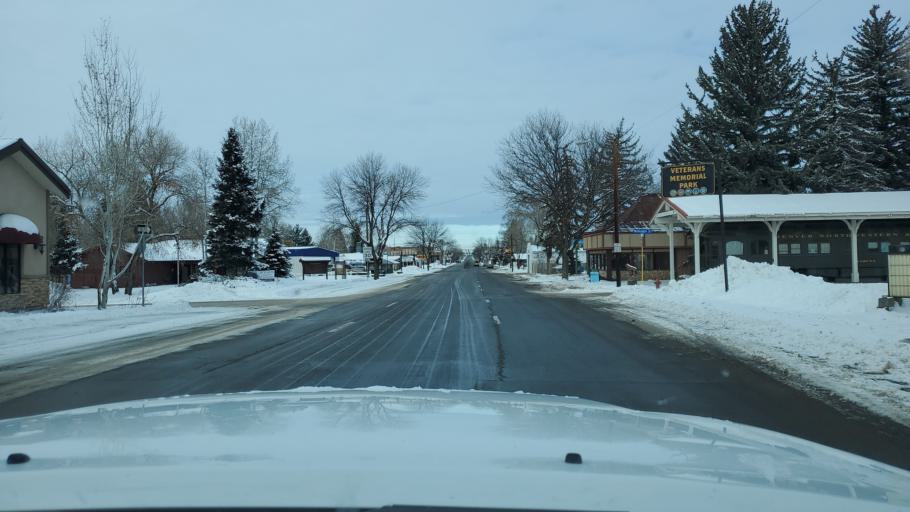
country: US
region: Colorado
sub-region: Moffat County
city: Craig
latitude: 40.5143
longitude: -107.5421
